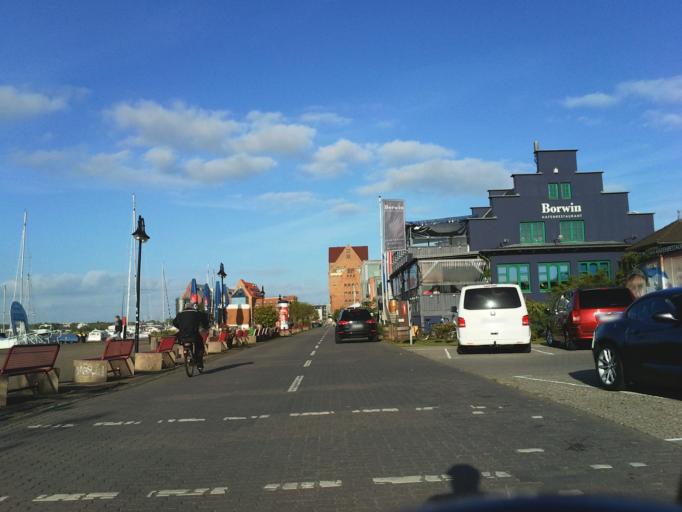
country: DE
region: Mecklenburg-Vorpommern
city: Rostock
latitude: 54.0926
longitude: 12.1369
